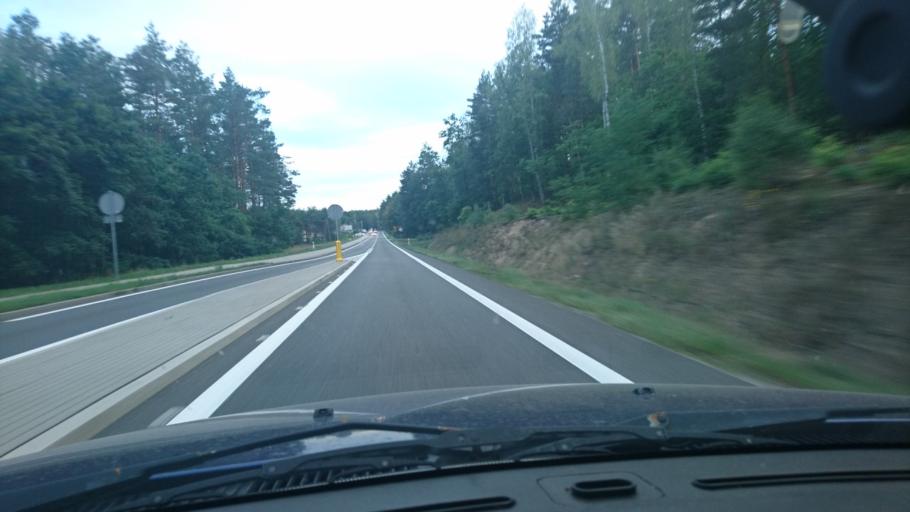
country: PL
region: Silesian Voivodeship
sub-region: Powiat tarnogorski
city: Tworog
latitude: 50.5955
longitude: 18.7021
